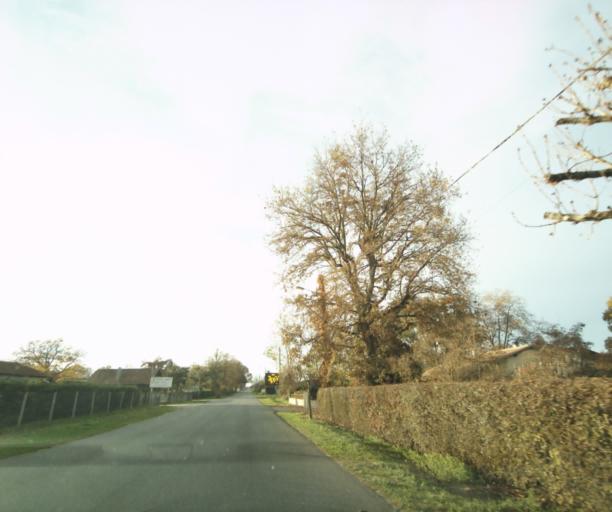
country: FR
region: Aquitaine
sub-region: Departement des Landes
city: Gabarret
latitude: 43.9879
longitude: 0.0018
